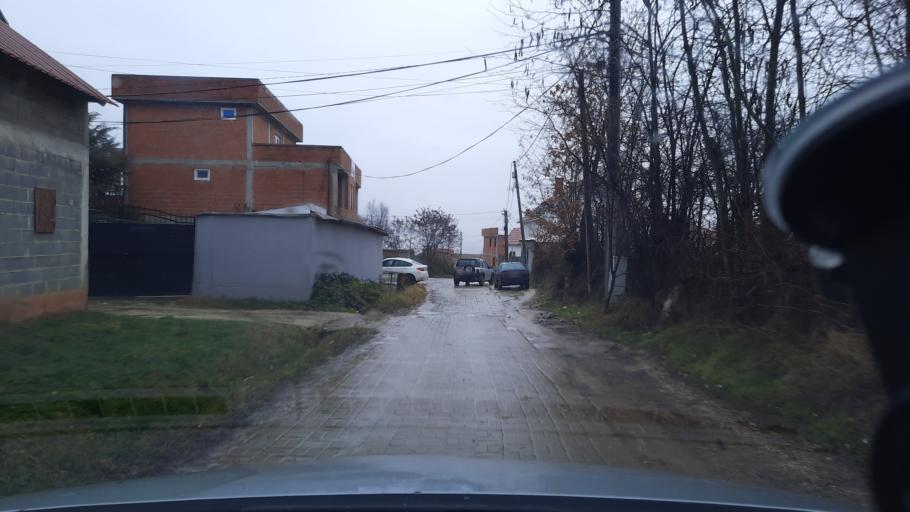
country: MK
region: Opstina Lipkovo
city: Matejche
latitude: 42.1238
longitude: 21.5995
